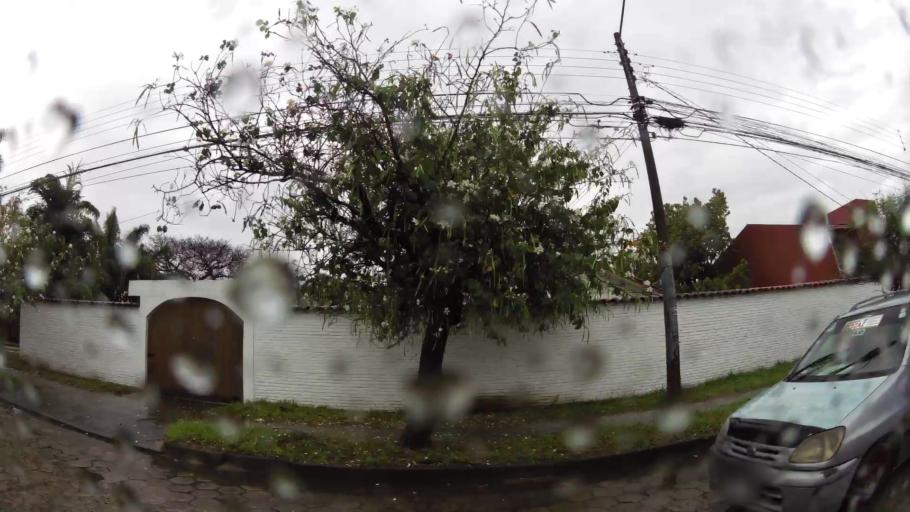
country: BO
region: Santa Cruz
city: Santa Cruz de la Sierra
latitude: -17.8019
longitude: -63.1744
